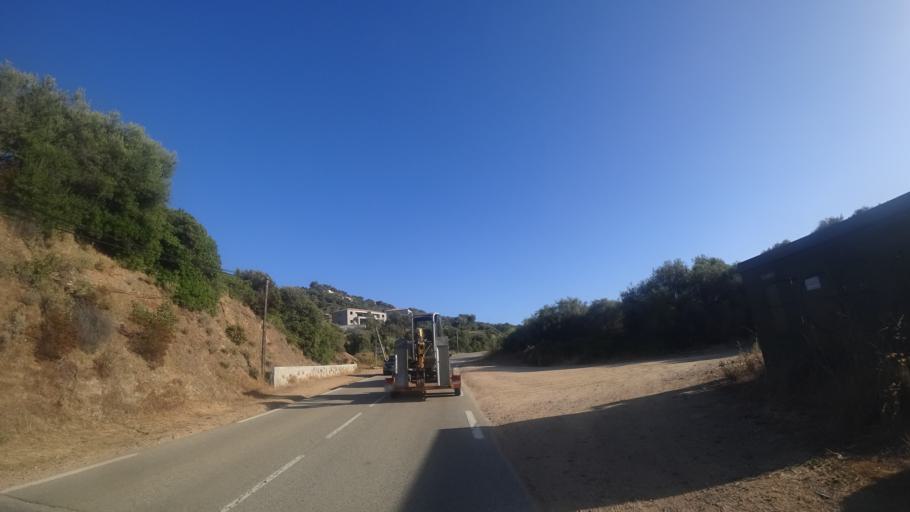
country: FR
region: Corsica
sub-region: Departement de la Corse-du-Sud
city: Cargese
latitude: 42.1463
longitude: 8.6032
